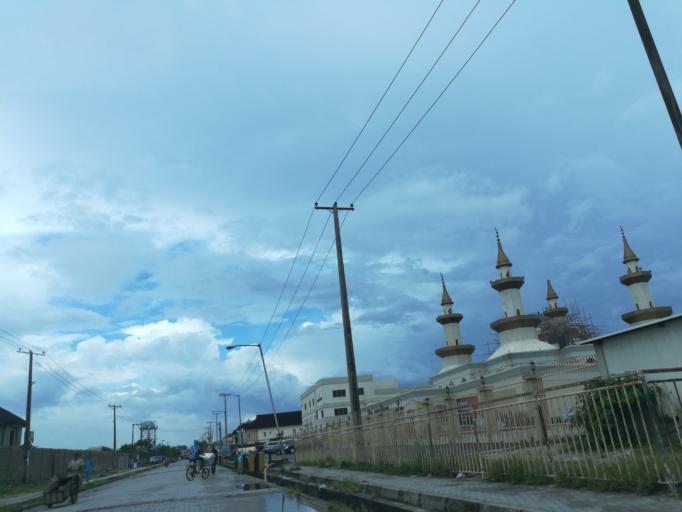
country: NG
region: Lagos
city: Ikoyi
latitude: 6.4378
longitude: 3.4746
